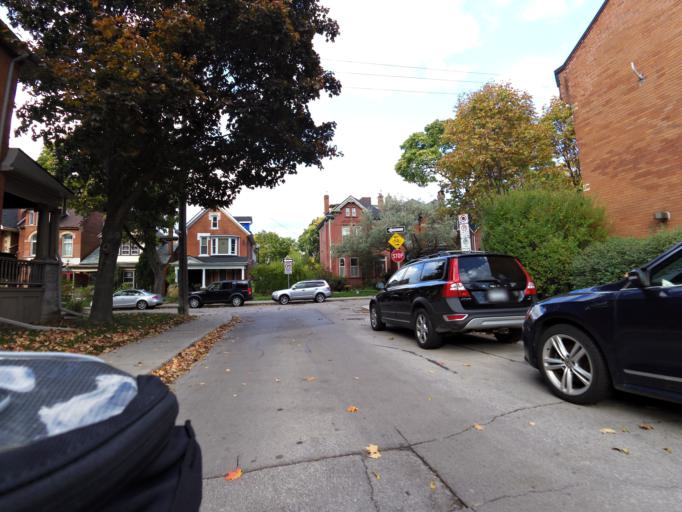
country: CA
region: Ontario
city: Hamilton
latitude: 43.2492
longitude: -79.8789
